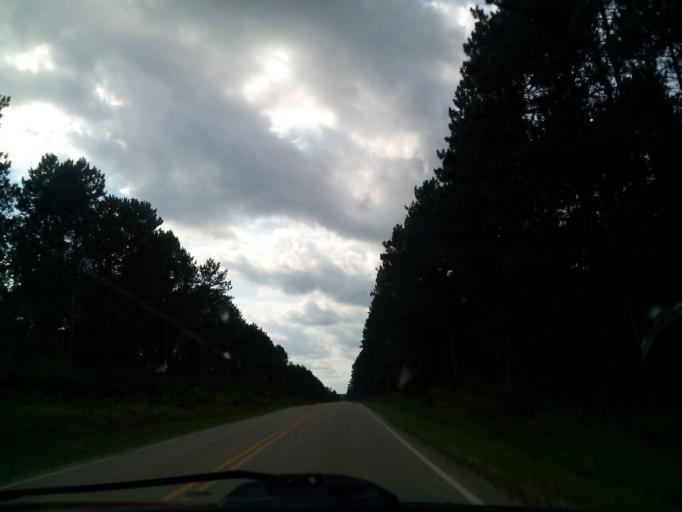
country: US
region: Michigan
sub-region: Dickinson County
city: Kingsford
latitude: 45.4021
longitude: -88.2232
